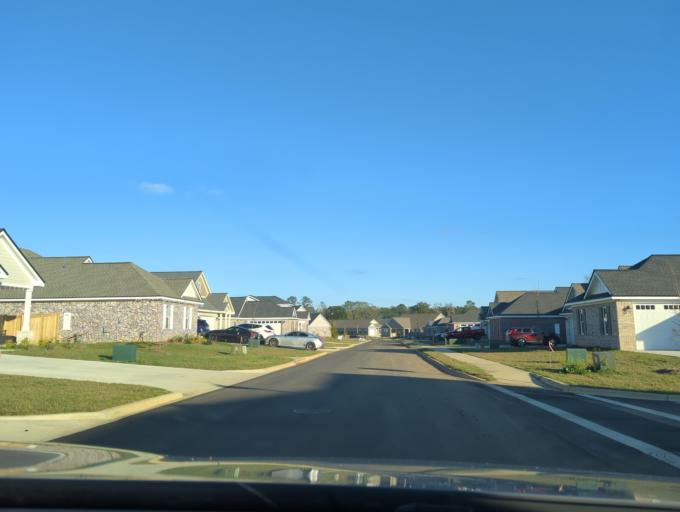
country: US
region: Florida
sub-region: Gadsden County
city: Midway
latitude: 30.5173
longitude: -84.3521
